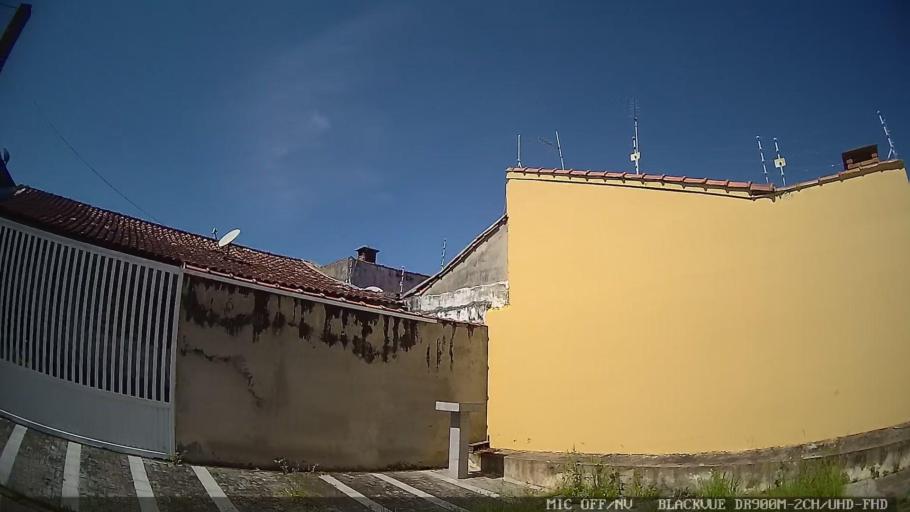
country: BR
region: Sao Paulo
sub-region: Peruibe
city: Peruibe
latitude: -24.3040
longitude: -46.9837
